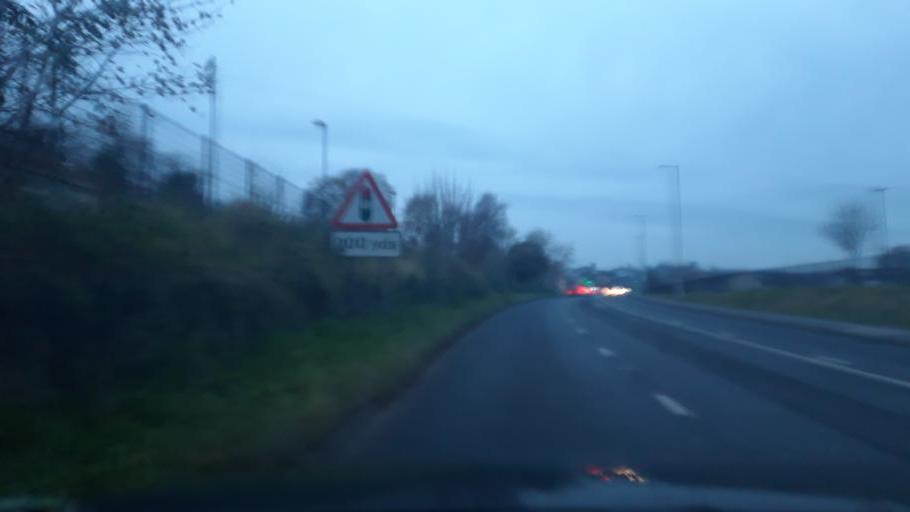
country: GB
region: Northern Ireland
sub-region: Newry and Mourne District
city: Newry
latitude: 54.1828
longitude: -6.3543
